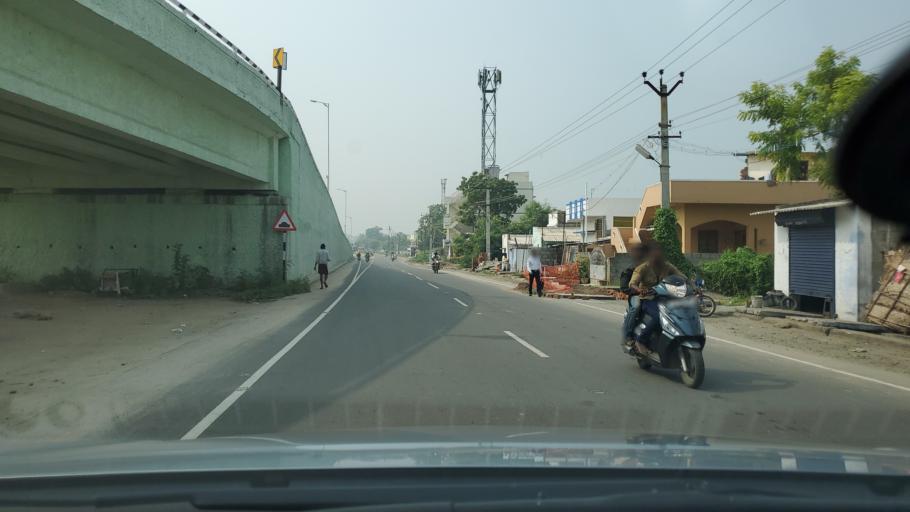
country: IN
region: Tamil Nadu
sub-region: Erode
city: Erode
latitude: 11.3188
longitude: 77.7133
